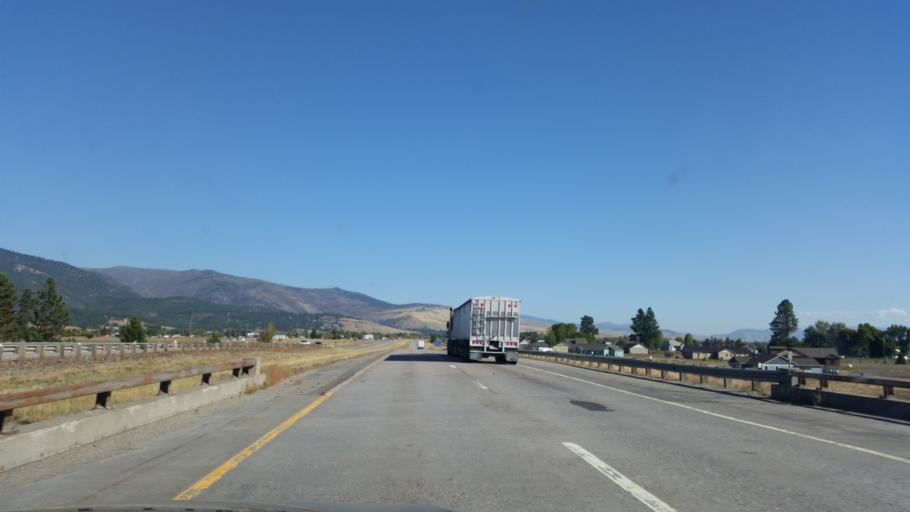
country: US
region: Montana
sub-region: Missoula County
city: Frenchtown
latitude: 47.0276
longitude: -114.2939
